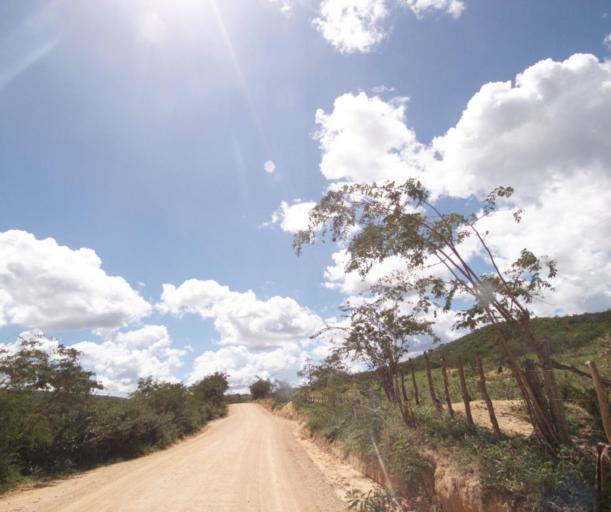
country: BR
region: Bahia
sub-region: Pocoes
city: Pocoes
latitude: -14.3014
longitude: -40.6264
